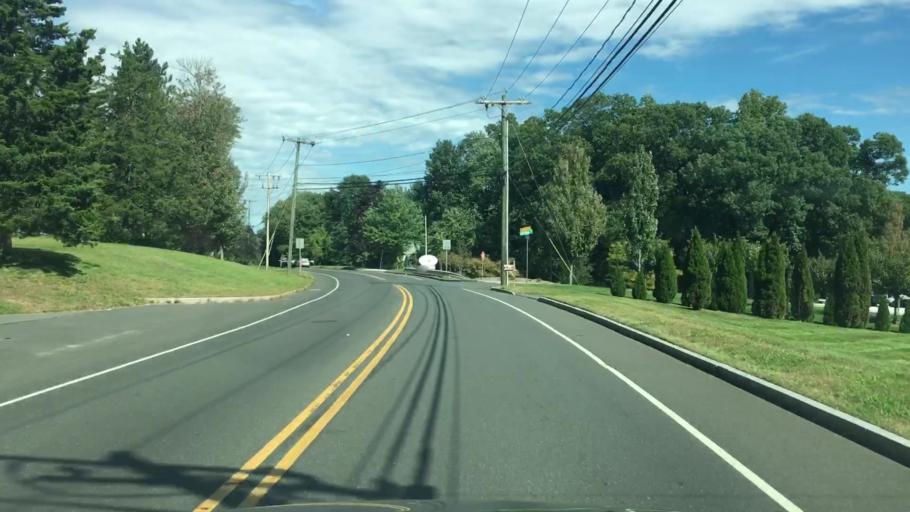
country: US
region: Connecticut
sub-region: Hartford County
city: Manchester
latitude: 41.8000
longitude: -72.5376
